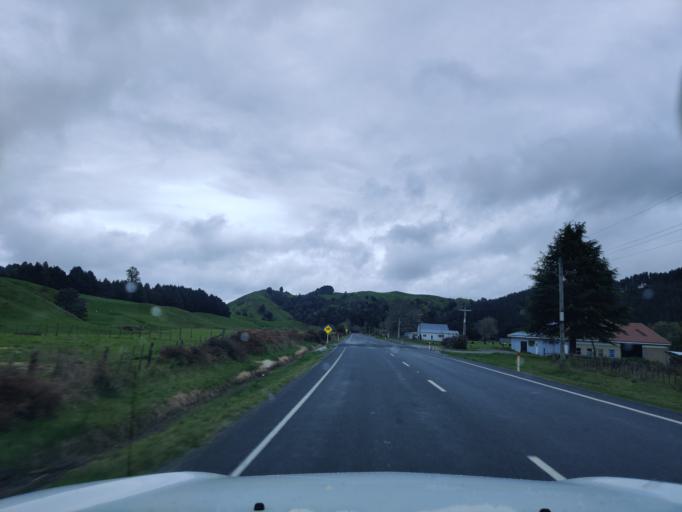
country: NZ
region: Waikato
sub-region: Otorohanga District
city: Otorohanga
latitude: -38.5798
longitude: 175.2155
